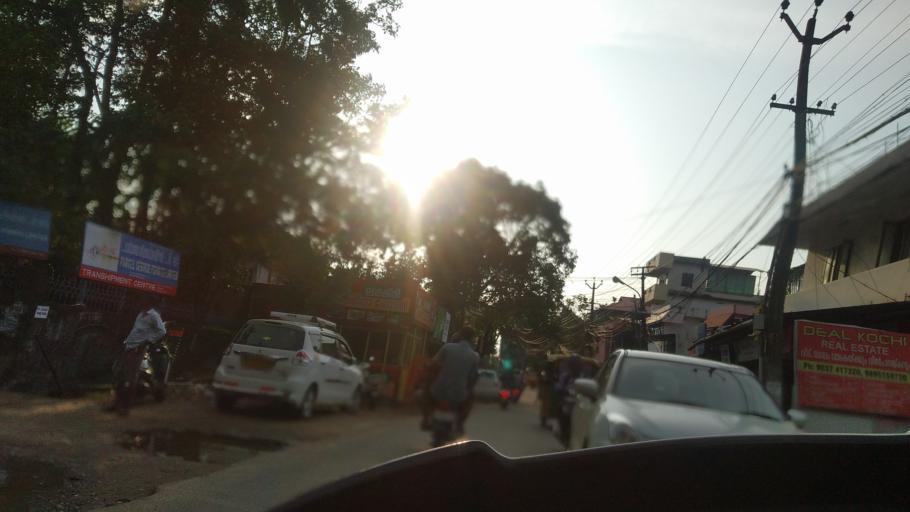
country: IN
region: Kerala
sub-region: Ernakulam
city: Cochin
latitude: 9.9858
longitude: 76.3083
